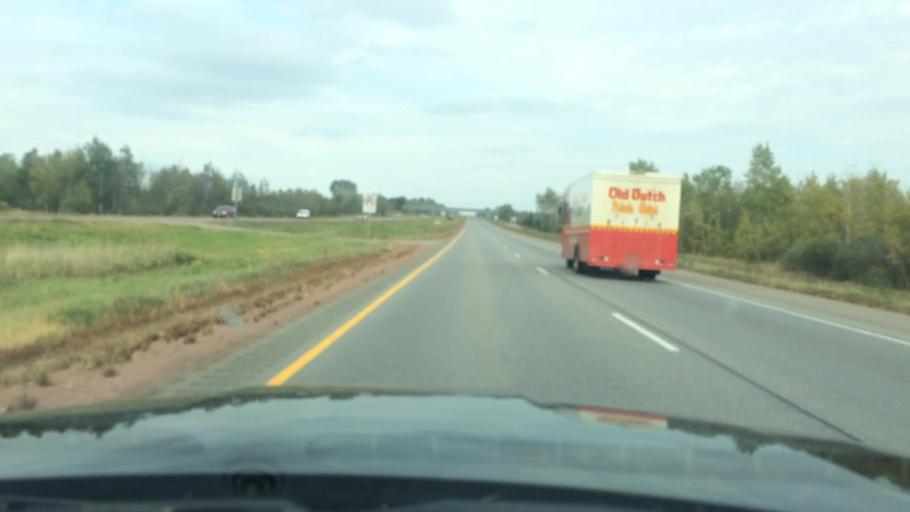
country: US
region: Wisconsin
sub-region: Marathon County
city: Mosinee
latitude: 44.7362
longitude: -89.6797
